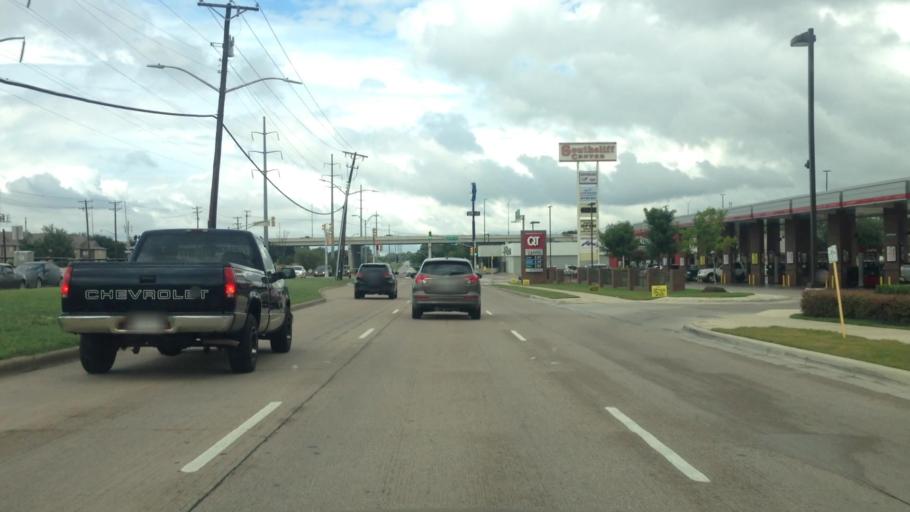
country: US
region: Texas
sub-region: Tarrant County
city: Edgecliff Village
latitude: 32.6726
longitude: -97.3836
